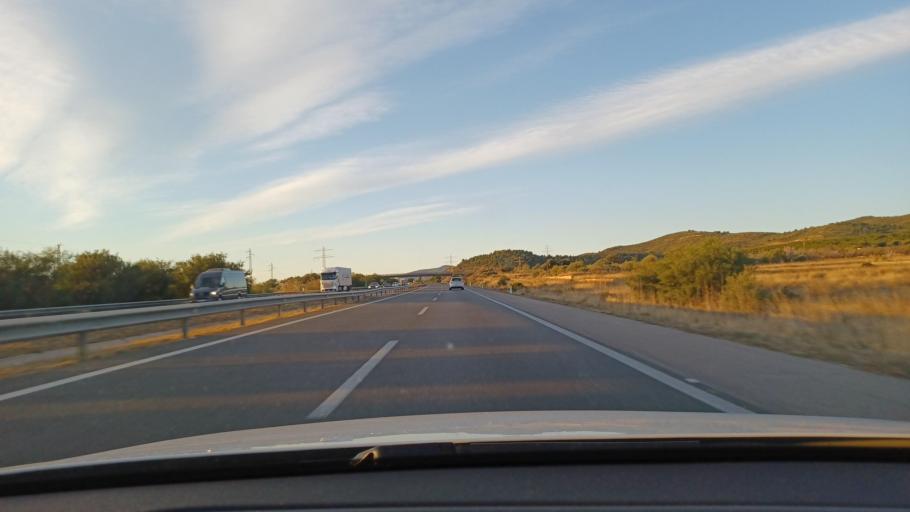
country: ES
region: Valencia
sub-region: Provincia de Castello
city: Torreblanca
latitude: 40.1839
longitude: 0.1679
